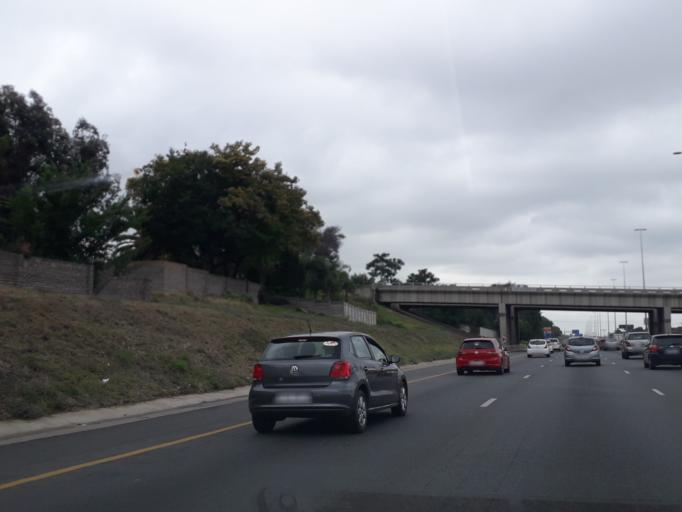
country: ZA
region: Gauteng
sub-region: City of Johannesburg Metropolitan Municipality
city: Roodepoort
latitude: -26.0929
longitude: 27.9673
